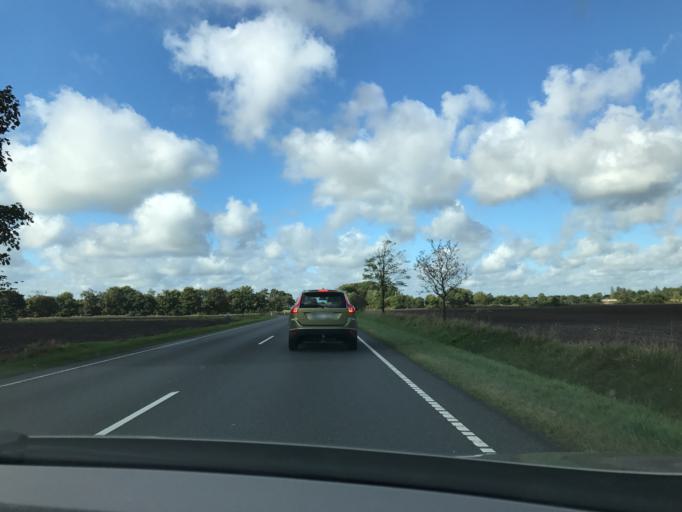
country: DK
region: South Denmark
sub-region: Billund Kommune
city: Billund
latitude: 55.7218
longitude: 9.1533
